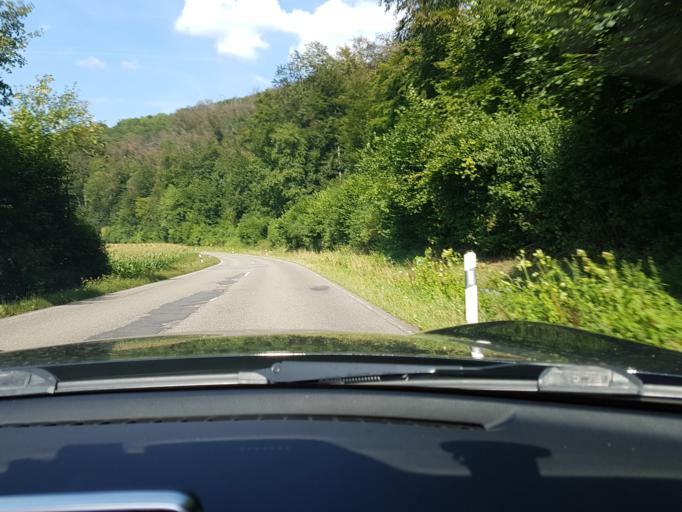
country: DE
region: Baden-Wuerttemberg
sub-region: Regierungsbezirk Stuttgart
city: Mockmuhl
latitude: 49.3408
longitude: 9.3560
